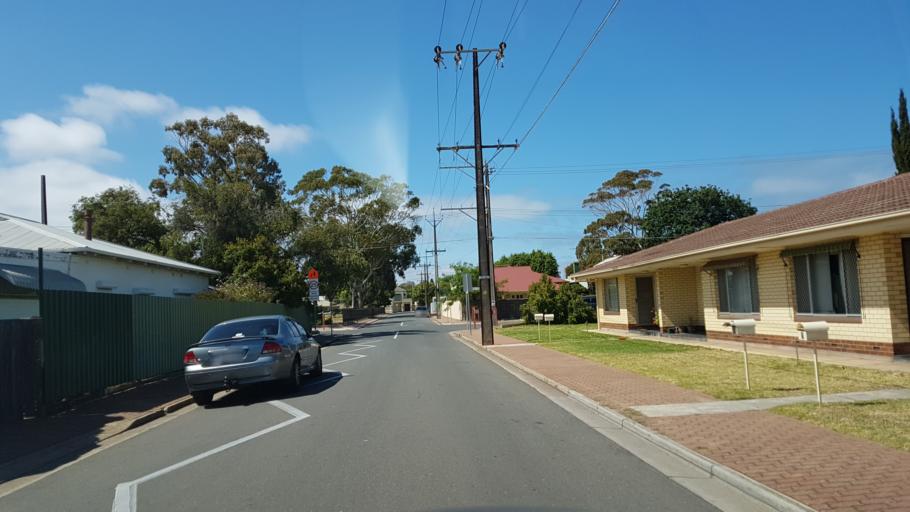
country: AU
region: South Australia
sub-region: Adelaide
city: Glenelg
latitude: -34.9715
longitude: 138.5188
